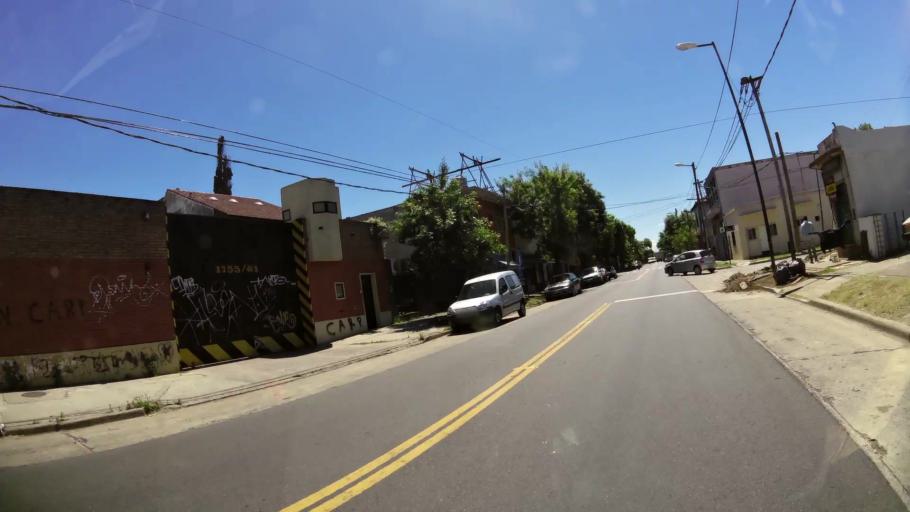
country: AR
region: Buenos Aires
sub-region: Partido de General San Martin
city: General San Martin
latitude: -34.5218
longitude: -58.5572
